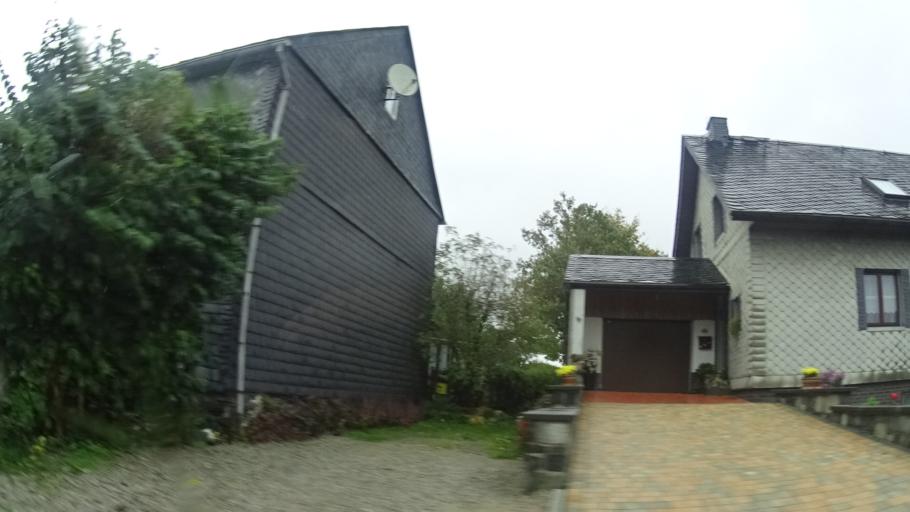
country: DE
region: Thuringia
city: Wurzbach
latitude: 50.4299
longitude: 11.4989
